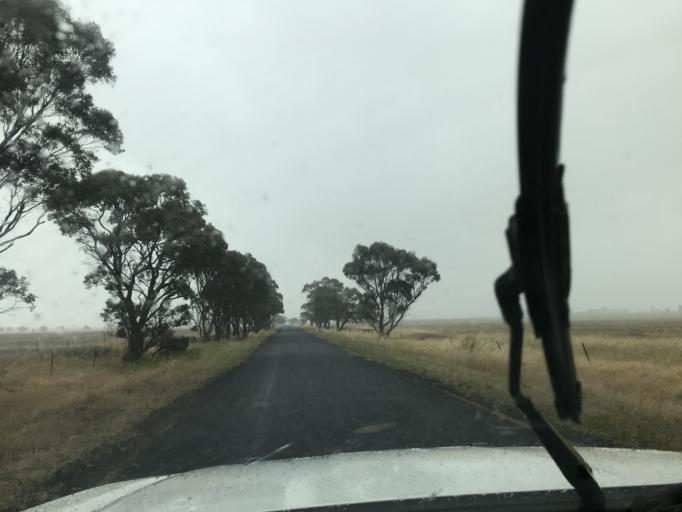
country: AU
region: South Australia
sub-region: Tatiara
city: Bordertown
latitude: -36.3143
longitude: 141.1563
